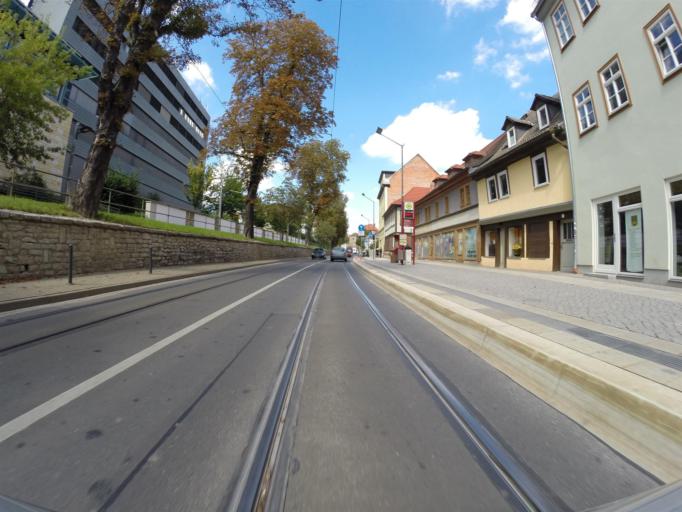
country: DE
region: Thuringia
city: Erfurt
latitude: 50.9809
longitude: 11.0219
